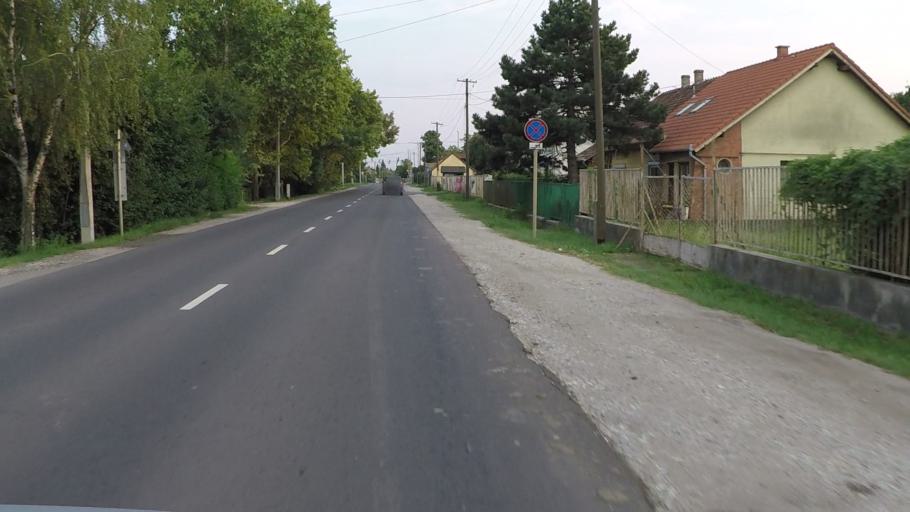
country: HU
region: Jasz-Nagykun-Szolnok
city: Szolnok
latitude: 47.1794
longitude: 20.1541
